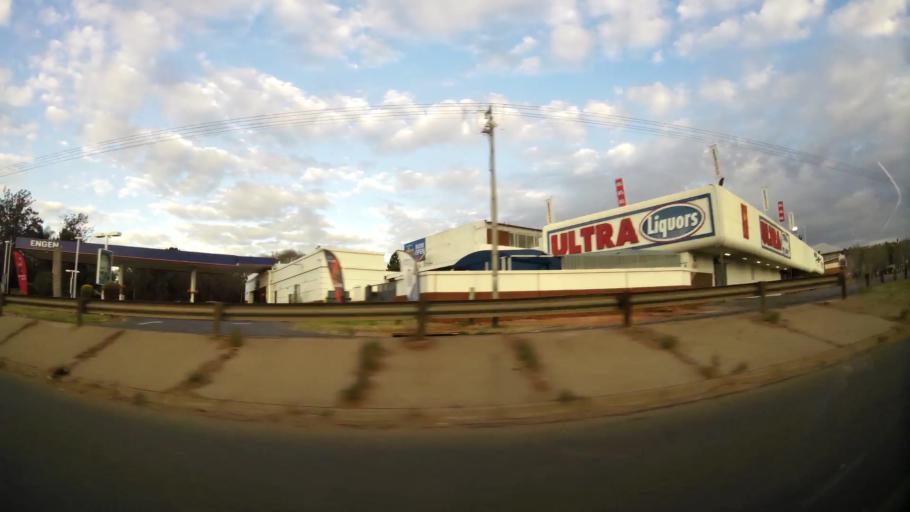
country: ZA
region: Gauteng
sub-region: City of Tshwane Metropolitan Municipality
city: Pretoria
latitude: -25.7383
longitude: 28.3115
